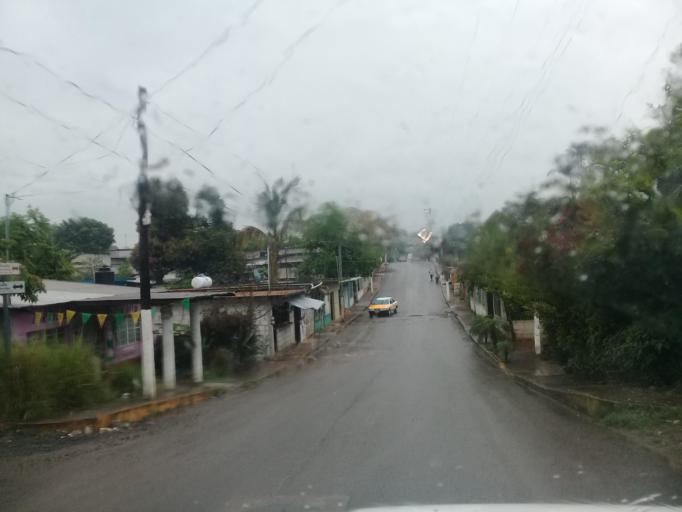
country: MX
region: Veracruz
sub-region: Cordoba
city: San Jose de Tapia
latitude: 18.8459
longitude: -96.9561
